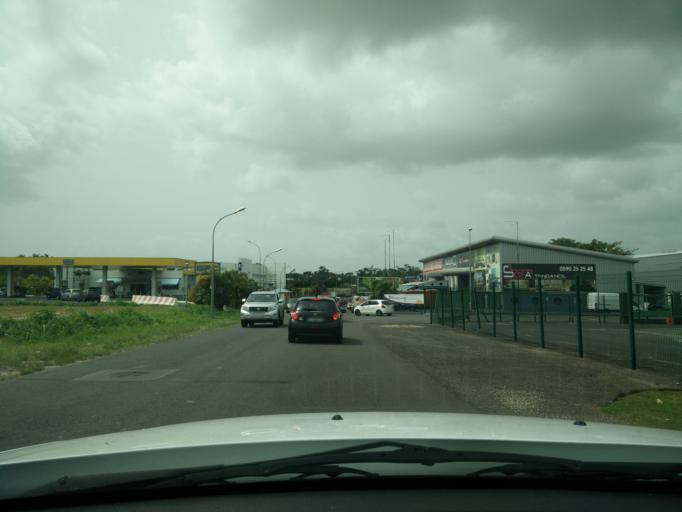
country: GP
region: Guadeloupe
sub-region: Guadeloupe
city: Baie-Mahault
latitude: 16.2447
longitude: -61.5710
